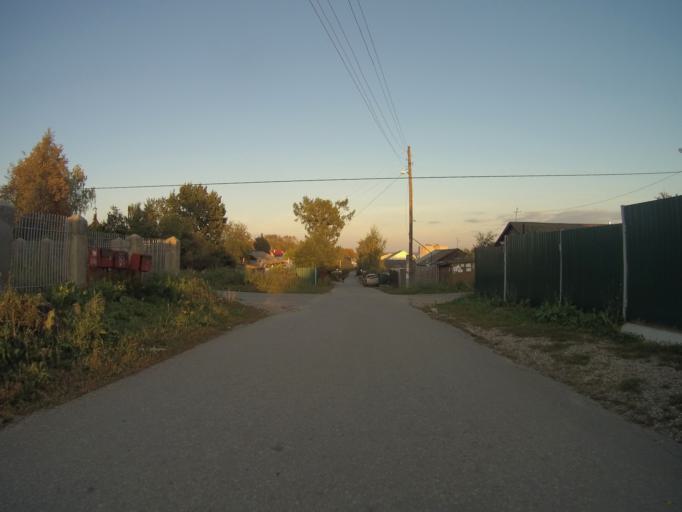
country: RU
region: Vladimir
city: Vladimir
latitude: 56.1144
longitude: 40.3644
